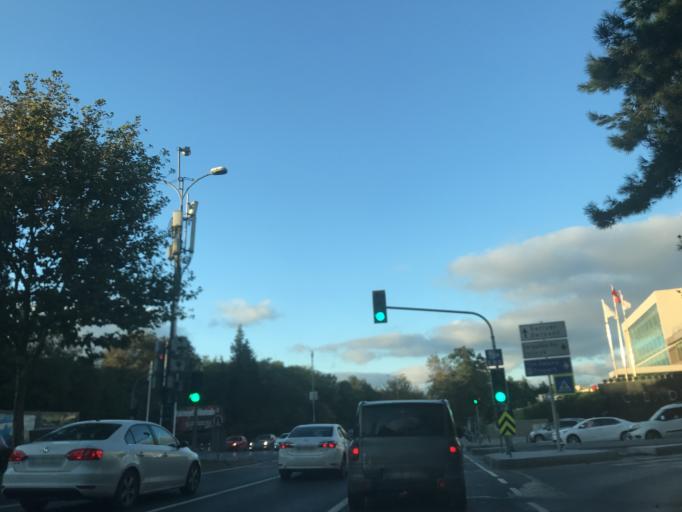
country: TR
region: Istanbul
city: Sisli
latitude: 41.1264
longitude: 29.0238
